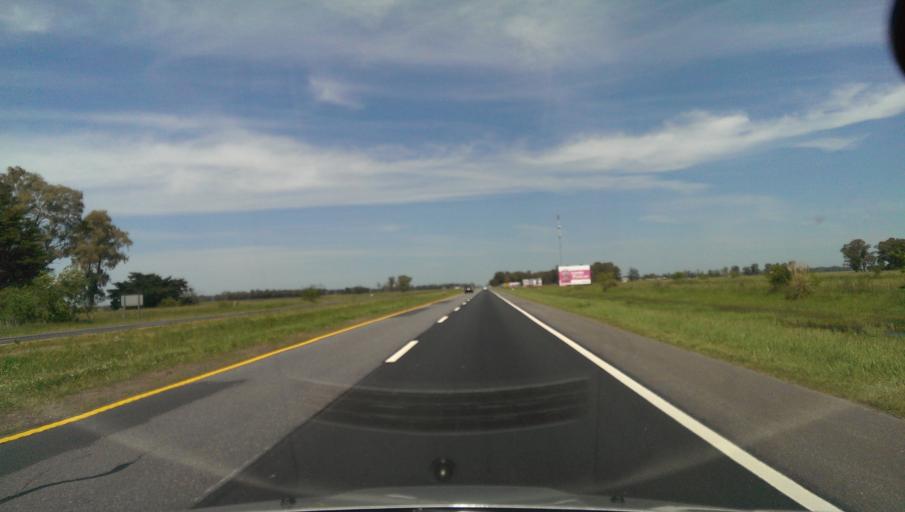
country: AR
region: Buenos Aires
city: San Miguel del Monte
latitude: -35.2704
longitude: -58.7680
